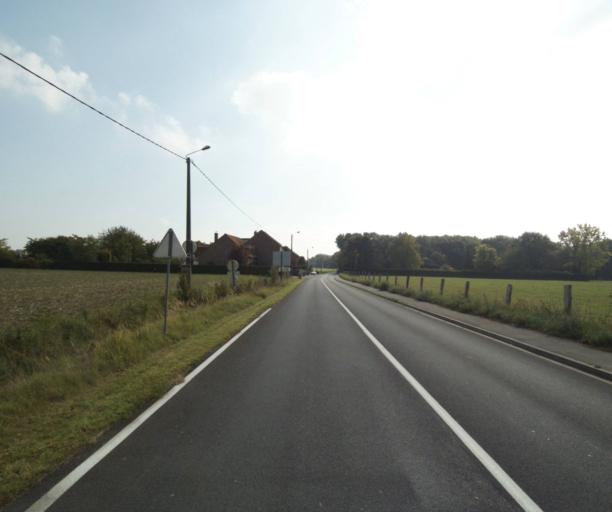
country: FR
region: Nord-Pas-de-Calais
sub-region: Departement du Nord
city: Houplin-Ancoisne
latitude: 50.5584
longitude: 3.0130
